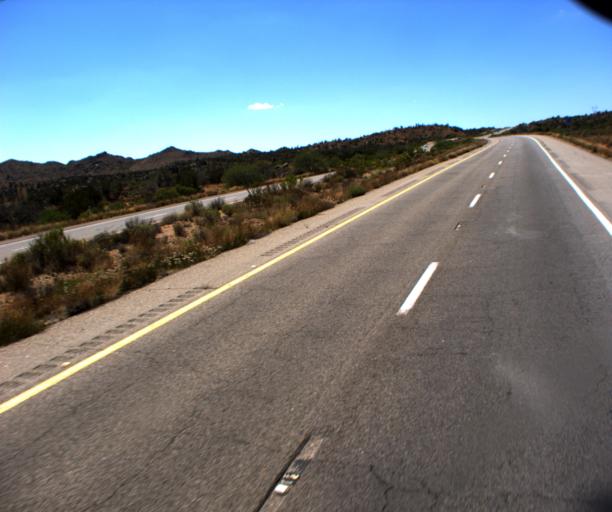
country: US
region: Arizona
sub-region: Yavapai County
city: Bagdad
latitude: 34.4655
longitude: -113.3055
